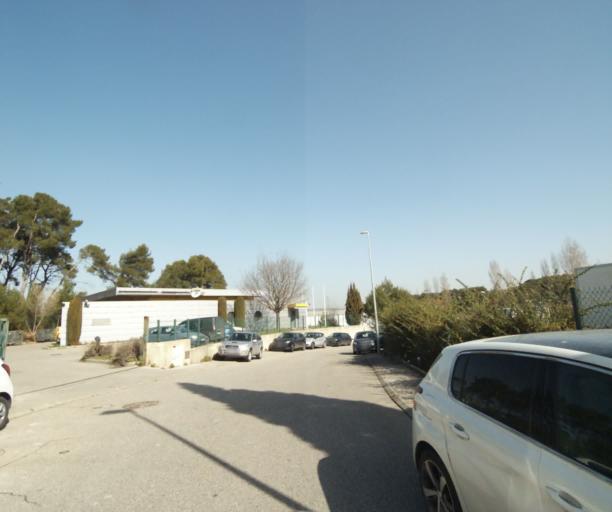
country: FR
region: Provence-Alpes-Cote d'Azur
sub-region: Departement des Bouches-du-Rhone
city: Cabries
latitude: 43.4267
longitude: 5.3960
